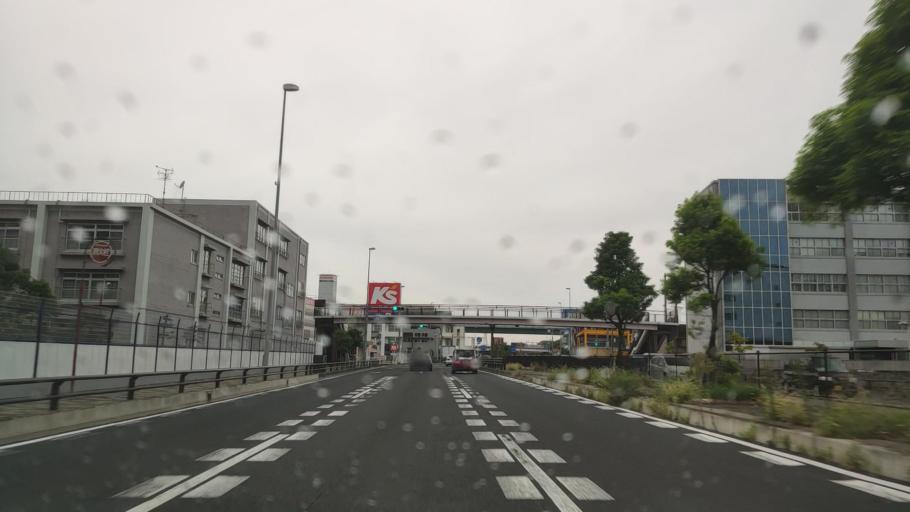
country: JP
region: Aichi
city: Nagoya-shi
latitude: 35.1999
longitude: 136.8814
